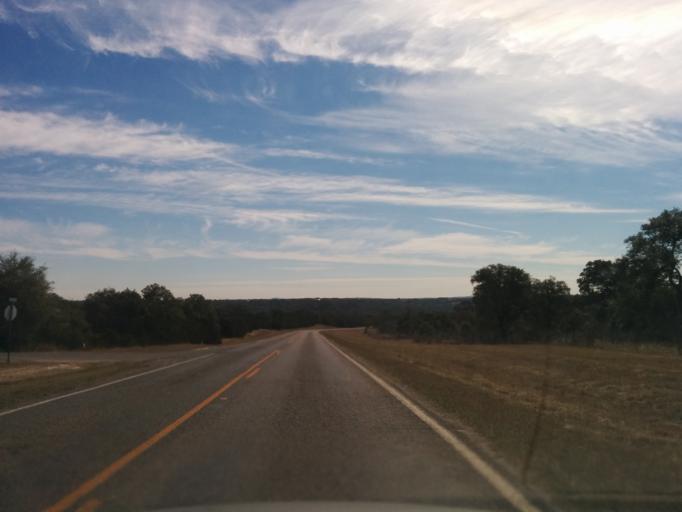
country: US
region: Texas
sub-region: Bexar County
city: Fair Oaks Ranch
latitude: 29.9016
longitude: -98.5649
